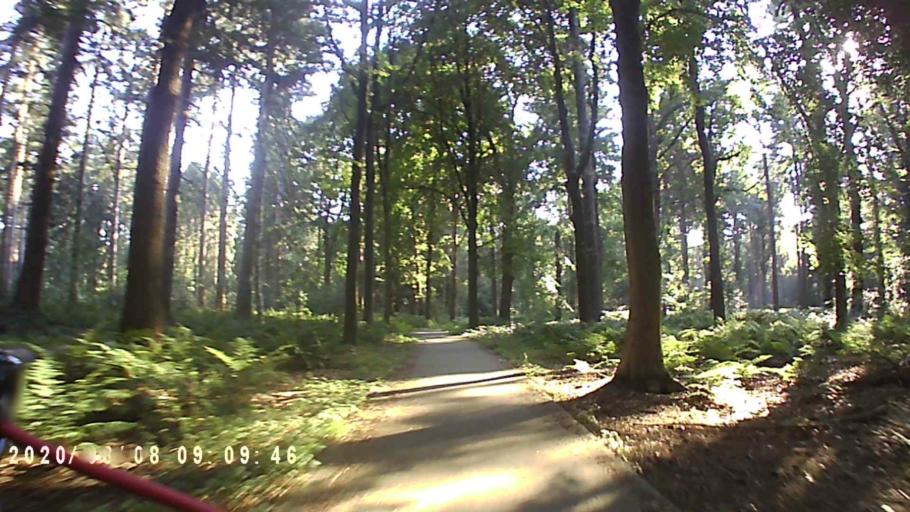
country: NL
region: Groningen
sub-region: Gemeente Leek
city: Leek
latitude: 53.0513
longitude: 6.3233
